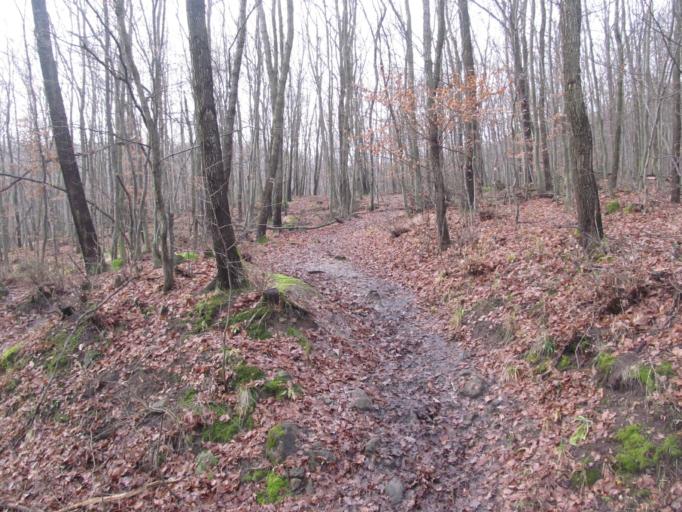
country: HU
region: Komarom-Esztergom
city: Pilismarot
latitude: 47.7410
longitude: 18.8777
